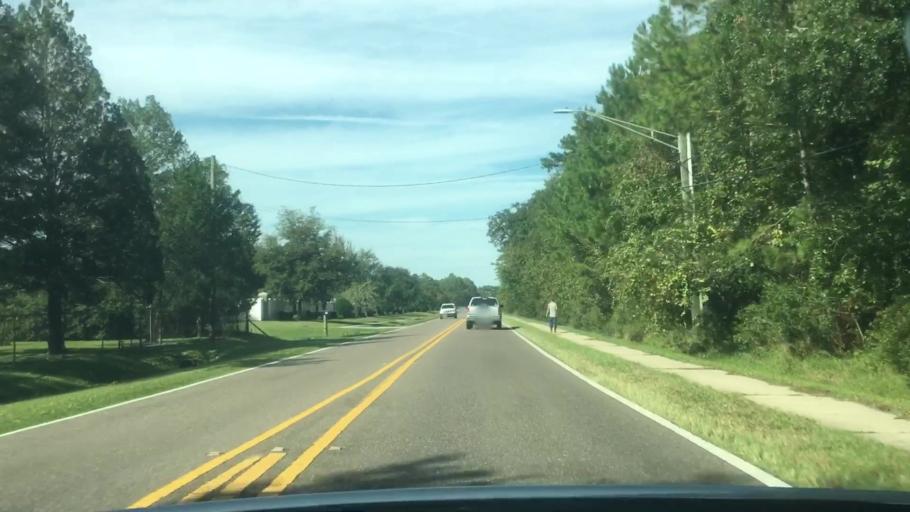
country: US
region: Florida
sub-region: Nassau County
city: Yulee
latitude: 30.4861
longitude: -81.6141
